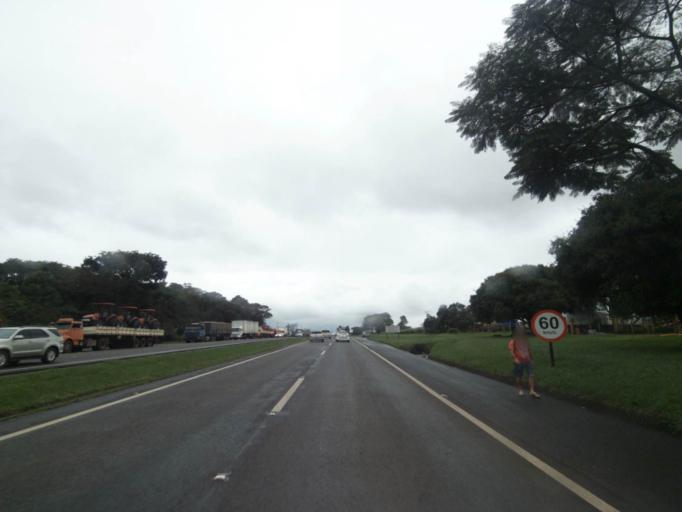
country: BR
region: Parana
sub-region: Foz Do Iguacu
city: Foz do Iguacu
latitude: -25.5102
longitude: -54.5648
